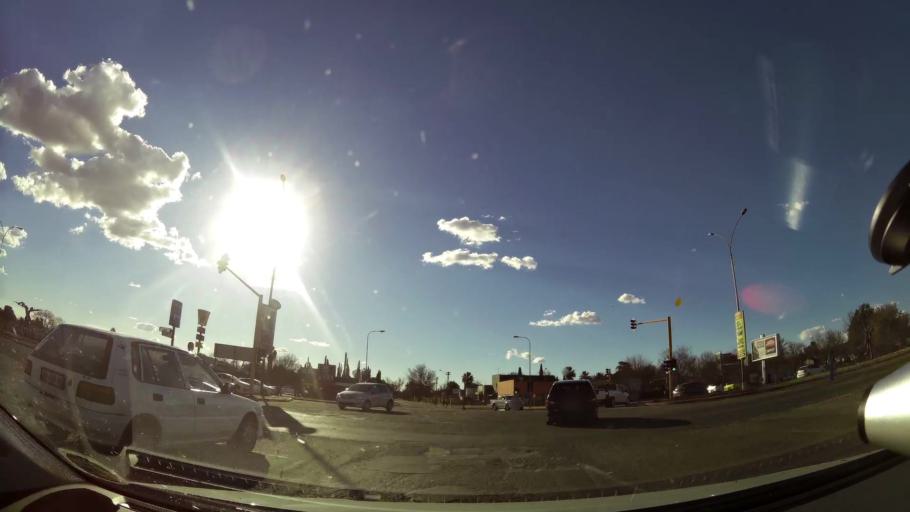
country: ZA
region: North-West
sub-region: Dr Kenneth Kaunda District Municipality
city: Klerksdorp
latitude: -26.8585
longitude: 26.6723
